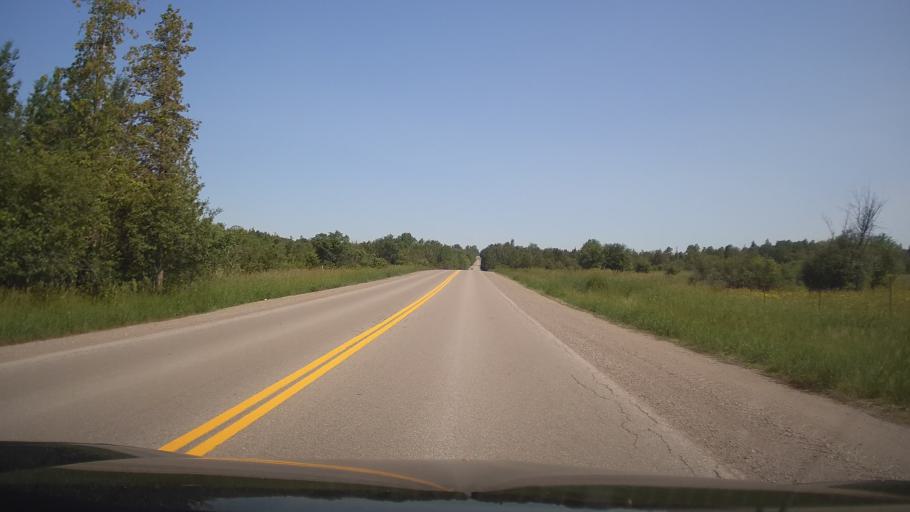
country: CA
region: Ontario
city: Uxbridge
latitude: 44.5146
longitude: -78.9576
